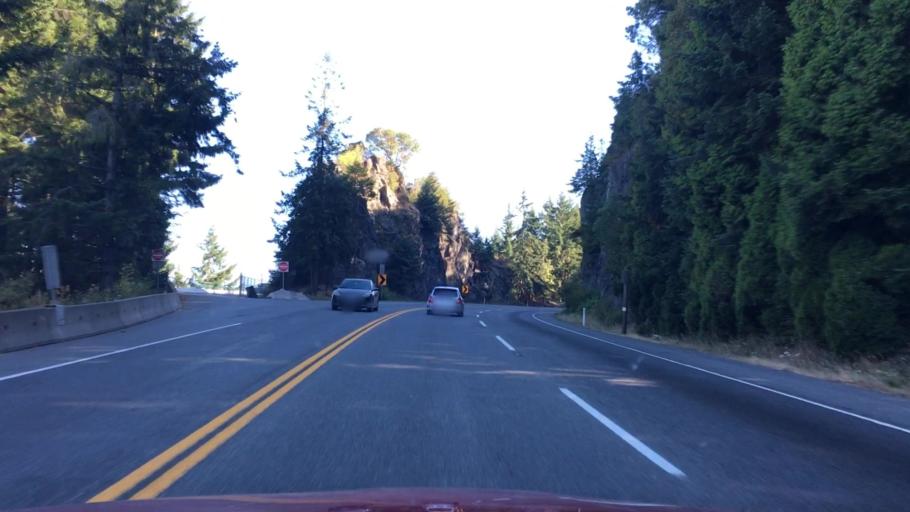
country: CA
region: British Columbia
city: North Saanich
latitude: 48.5855
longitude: -123.5302
